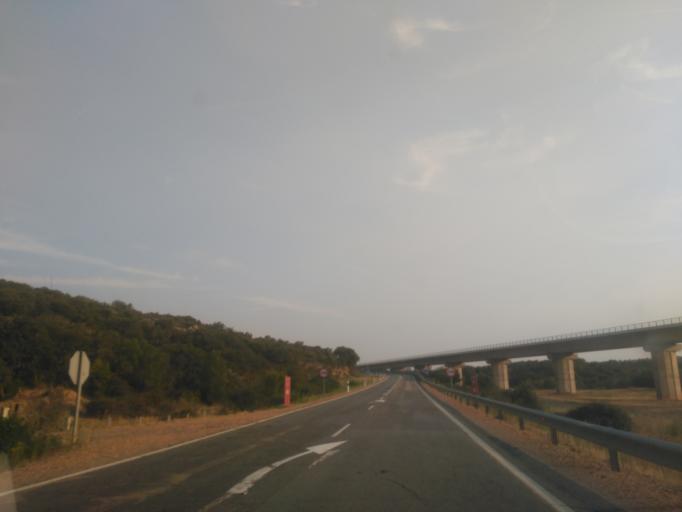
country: ES
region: Castille and Leon
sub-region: Provincia de Zamora
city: Perilla de Castro
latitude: 41.7524
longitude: -5.8548
